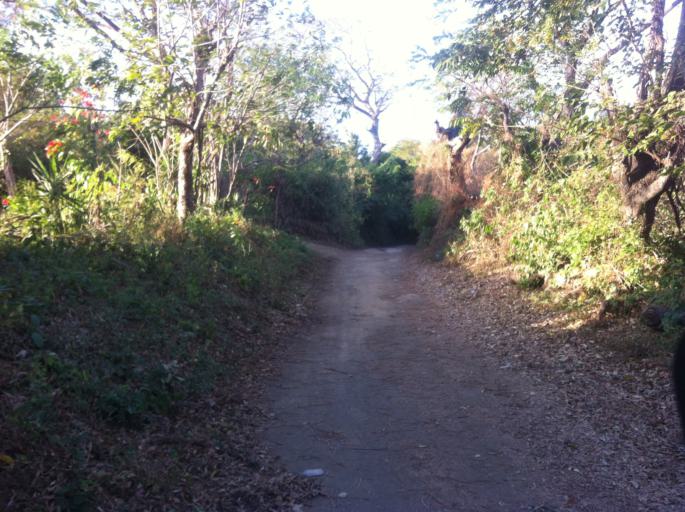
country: NI
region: Managua
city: El Crucero
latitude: 12.0727
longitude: -86.3098
